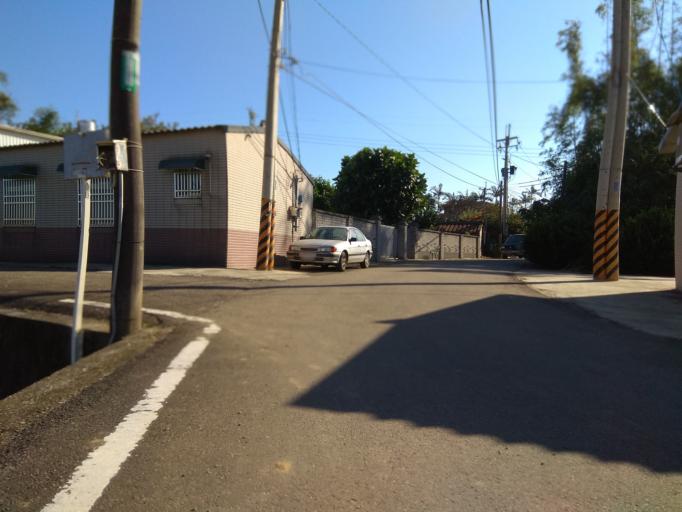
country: TW
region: Taiwan
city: Taoyuan City
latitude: 24.9786
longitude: 121.1841
